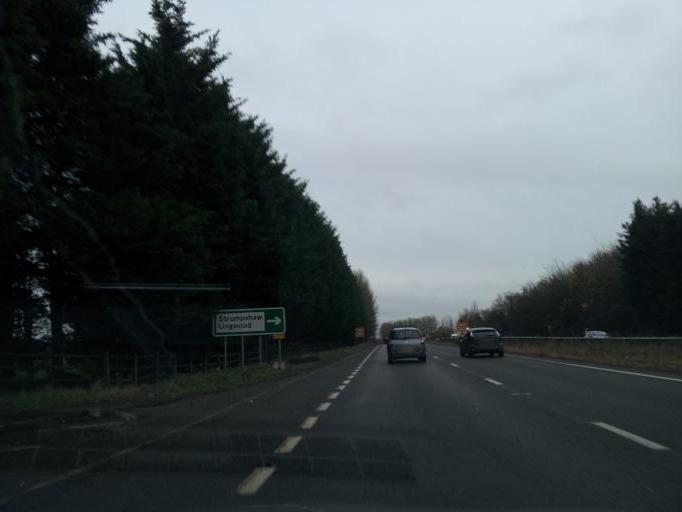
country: GB
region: England
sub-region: Norfolk
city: Brundall
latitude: 52.6377
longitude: 1.4558
